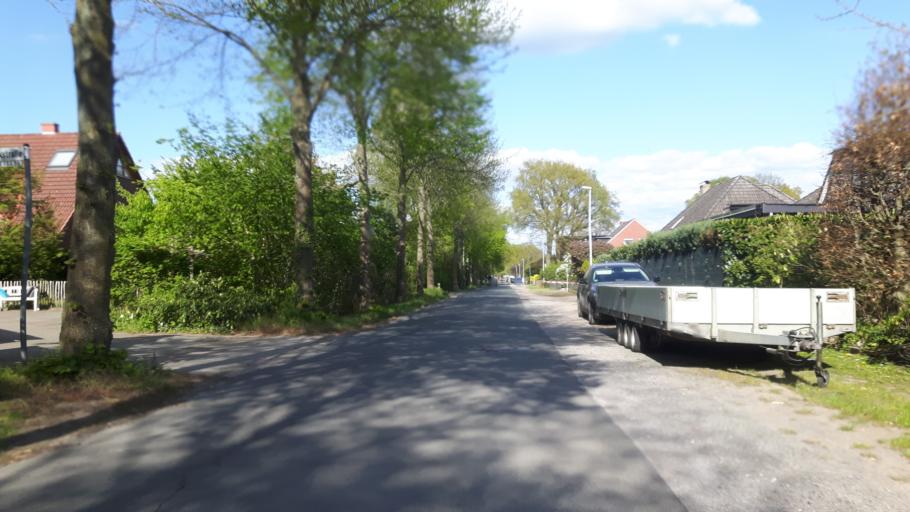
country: DE
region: Lower Saxony
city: Kirchseelte
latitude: 52.9911
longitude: 8.6904
